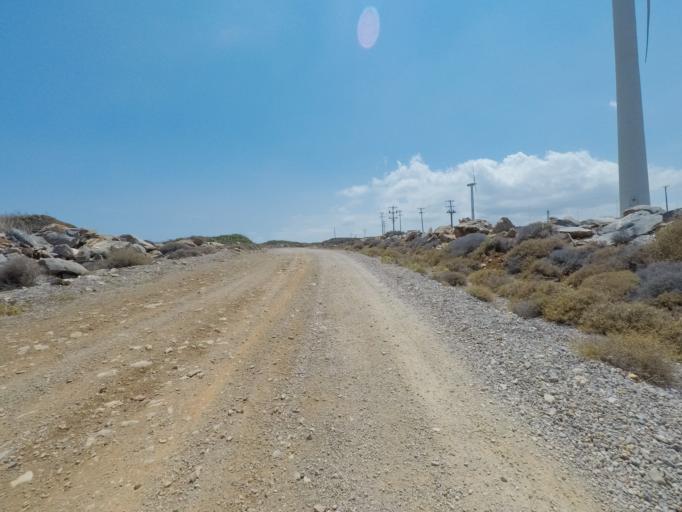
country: GR
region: Crete
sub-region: Nomos Lasithiou
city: Elounda
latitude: 35.3258
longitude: 25.7553
